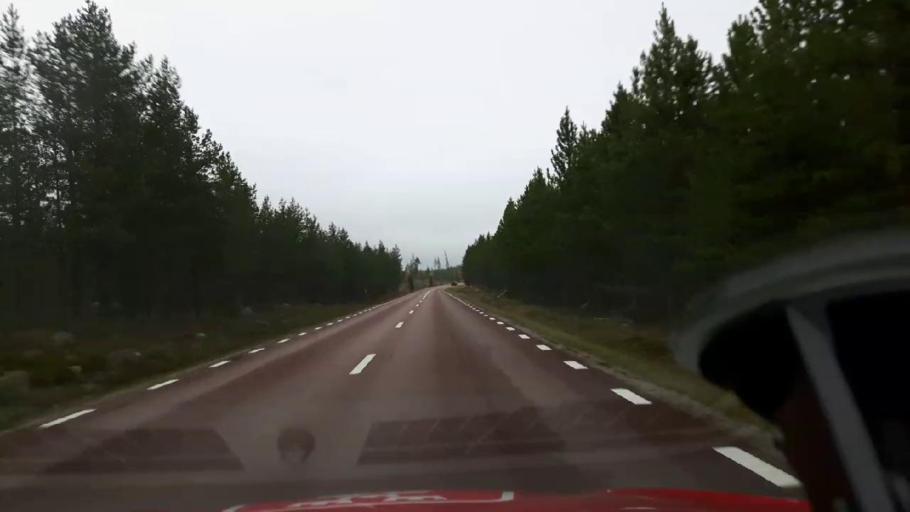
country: SE
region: Jaemtland
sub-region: Bergs Kommun
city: Hoverberg
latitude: 62.4334
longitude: 14.5932
